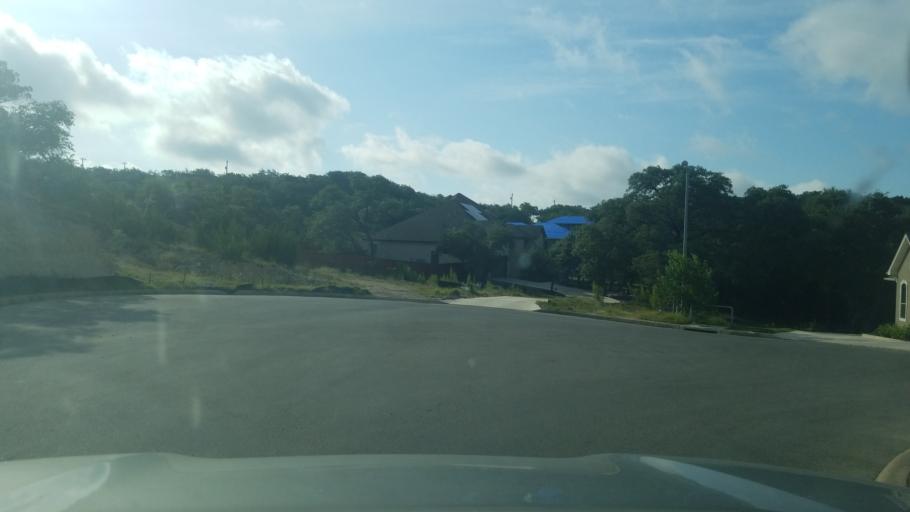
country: US
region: Texas
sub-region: Bexar County
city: Timberwood Park
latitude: 29.6888
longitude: -98.5177
